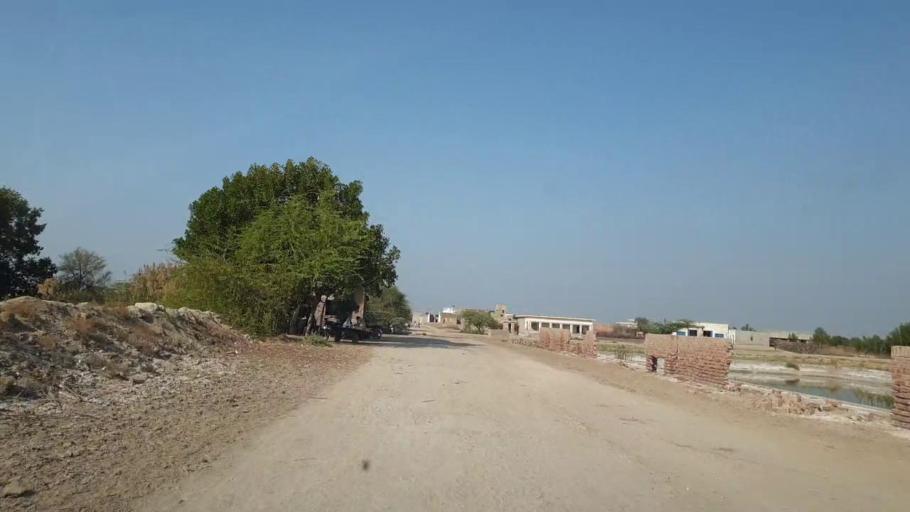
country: PK
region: Sindh
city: Tando Mittha Khan
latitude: 25.7511
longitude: 69.1970
